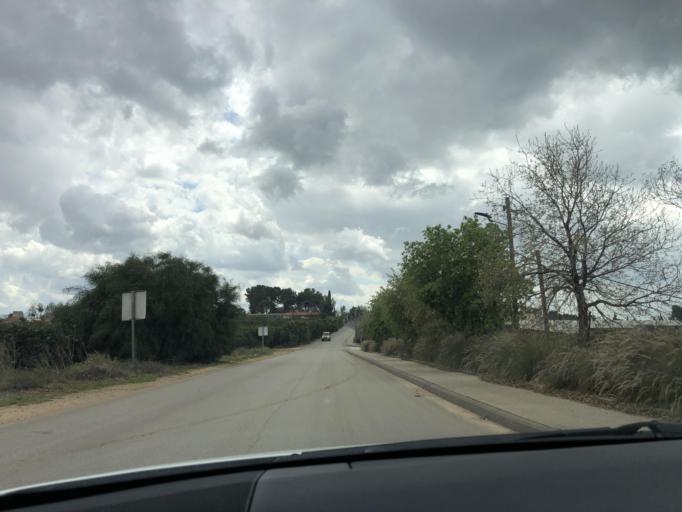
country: IL
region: Central District
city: Tel Mond
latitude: 32.2711
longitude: 34.9357
